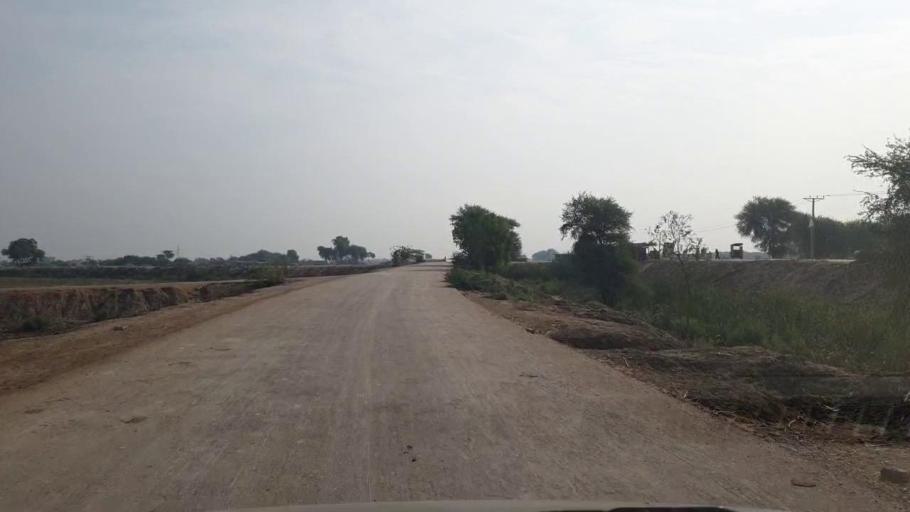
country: PK
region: Sindh
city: Tando Muhammad Khan
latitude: 25.1264
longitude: 68.5140
